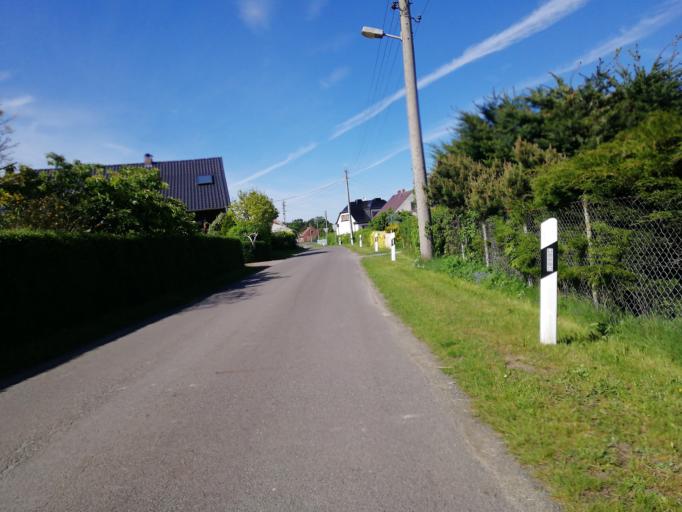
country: DE
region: Brandenburg
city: Calau
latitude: 51.7445
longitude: 13.9203
